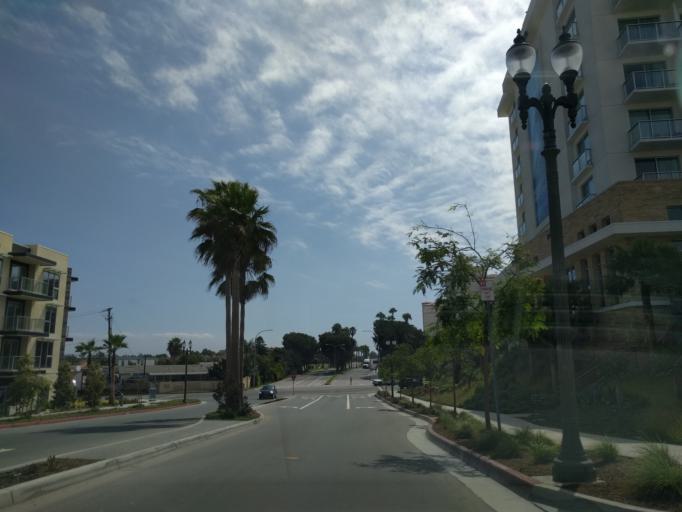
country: US
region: California
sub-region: Orange County
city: Huntington Beach
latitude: 33.6547
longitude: -117.9958
